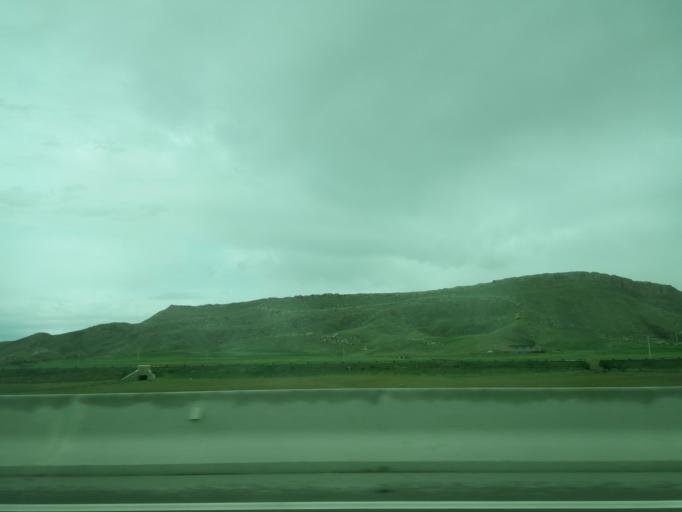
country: DZ
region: Medea
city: Ksar el Boukhari
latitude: 35.8197
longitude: 2.7676
